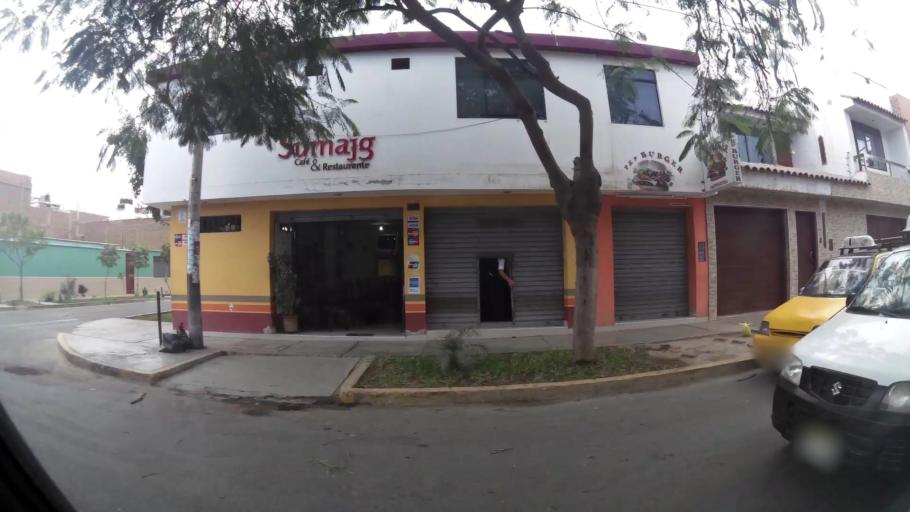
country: PE
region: La Libertad
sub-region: Provincia de Trujillo
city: Trujillo
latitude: -8.0957
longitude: -79.0223
